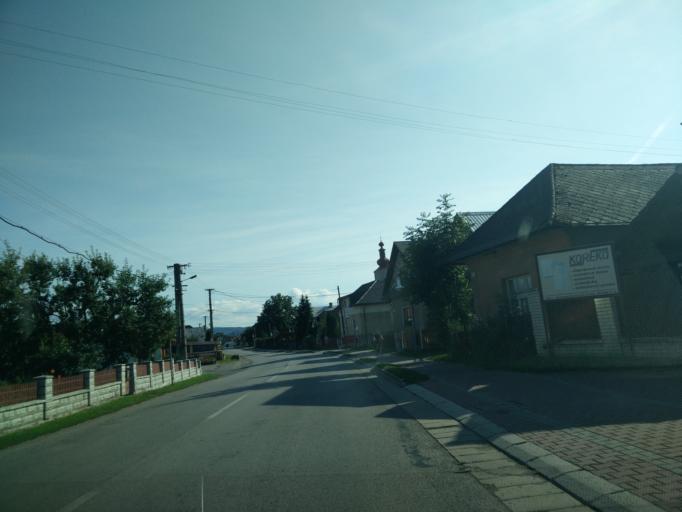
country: SK
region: Nitriansky
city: Handlova
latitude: 48.9106
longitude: 18.7596
